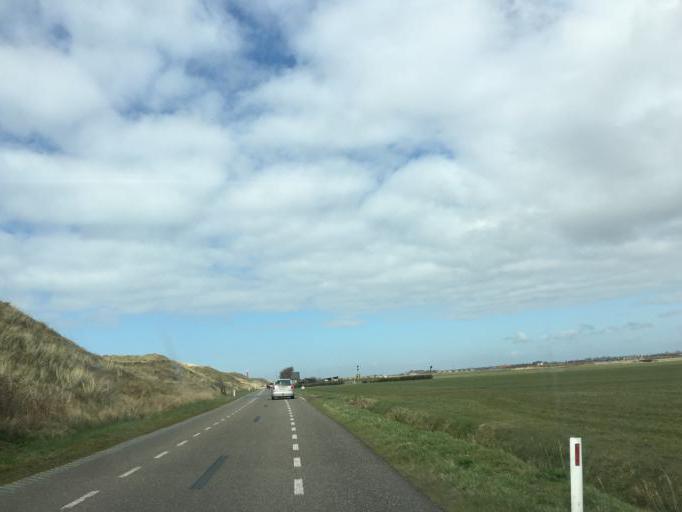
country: NL
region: North Holland
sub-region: Gemeente Den Helder
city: Den Helder
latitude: 52.8705
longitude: 4.7143
